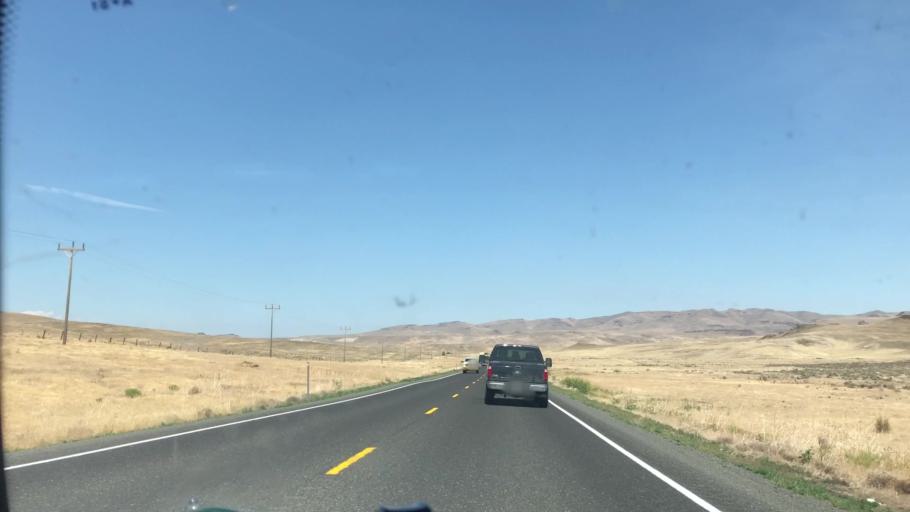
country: US
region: Idaho
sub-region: Owyhee County
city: Marsing
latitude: 43.2439
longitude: -117.0375
